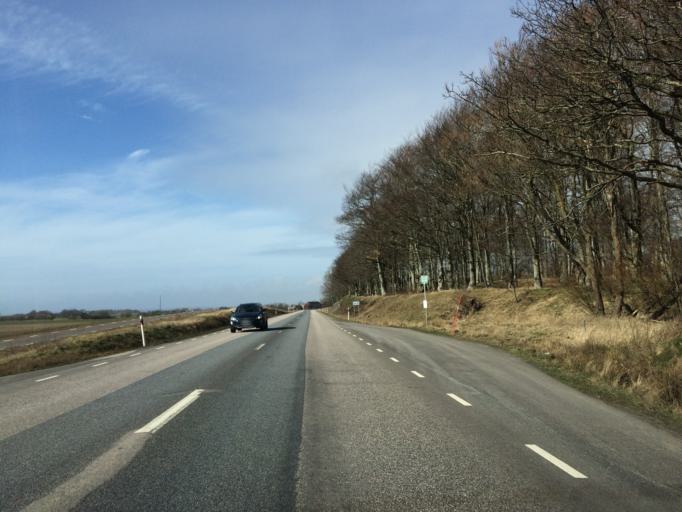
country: SE
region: Halland
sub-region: Halmstads Kommun
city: Paarp
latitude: 56.6017
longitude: 12.9661
